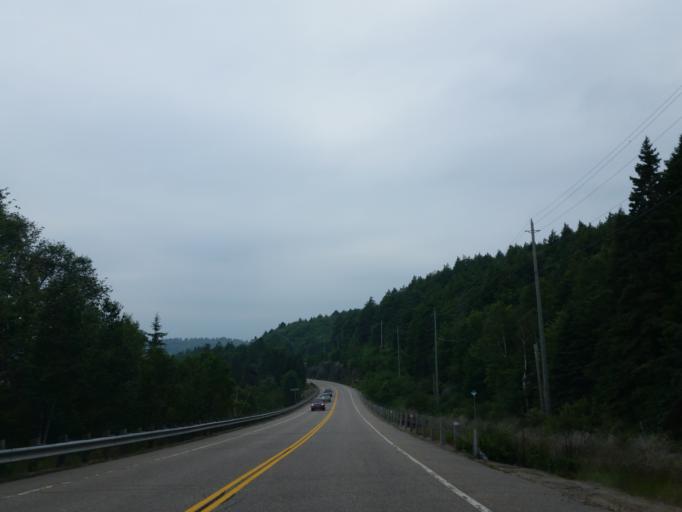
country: CA
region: Ontario
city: Mattawa
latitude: 45.5816
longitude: -78.4635
